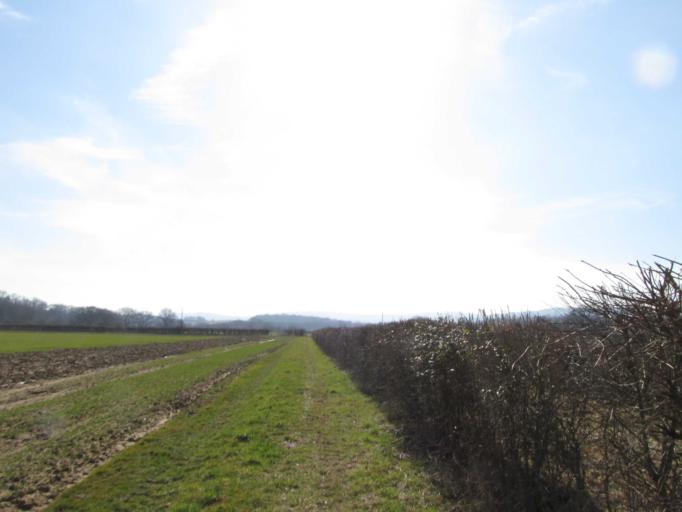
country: GB
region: England
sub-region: West Sussex
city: Petworth
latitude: 50.9693
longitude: -0.6047
